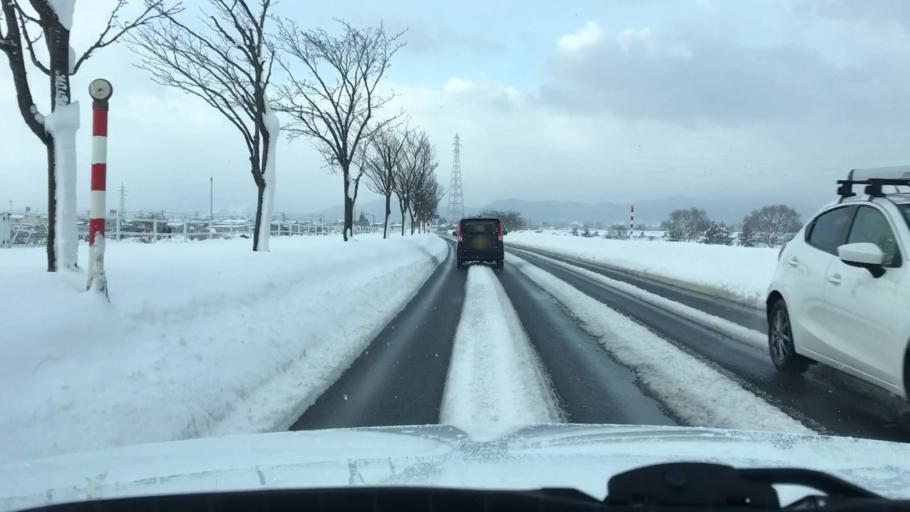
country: JP
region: Aomori
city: Hirosaki
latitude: 40.6321
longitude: 140.4730
